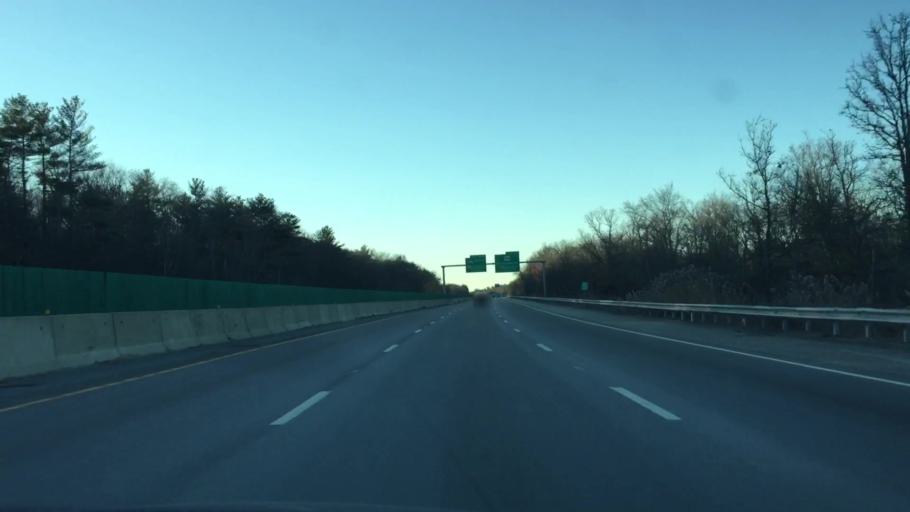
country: US
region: Massachusetts
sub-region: Plymouth County
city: West Bridgewater
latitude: 41.9796
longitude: -71.0255
